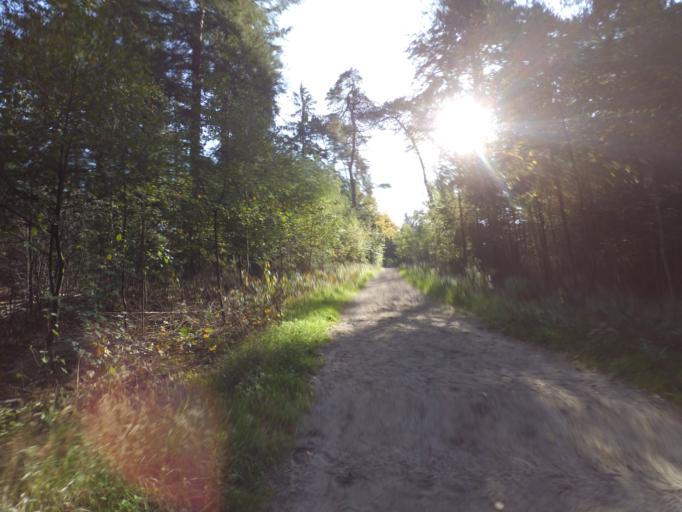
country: NL
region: Utrecht
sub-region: Gemeente Zeist
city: Zeist
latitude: 52.1145
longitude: 5.2198
